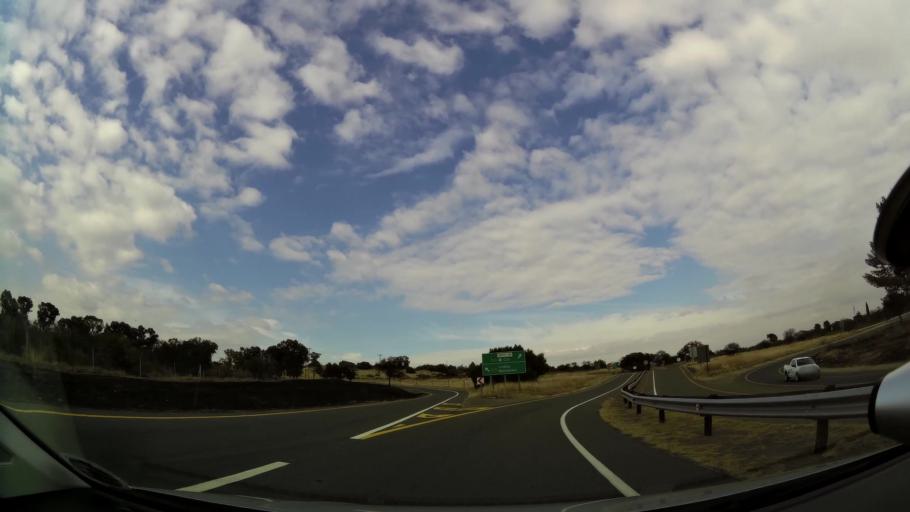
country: ZA
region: Orange Free State
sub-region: Fezile Dabi District Municipality
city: Kroonstad
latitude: -27.6872
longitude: 27.2434
